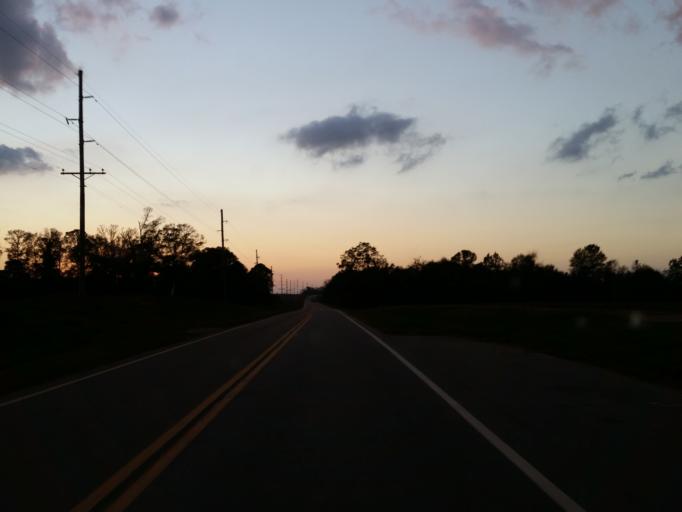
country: US
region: Georgia
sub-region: Dooly County
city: Vienna
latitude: 32.1236
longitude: -83.7302
